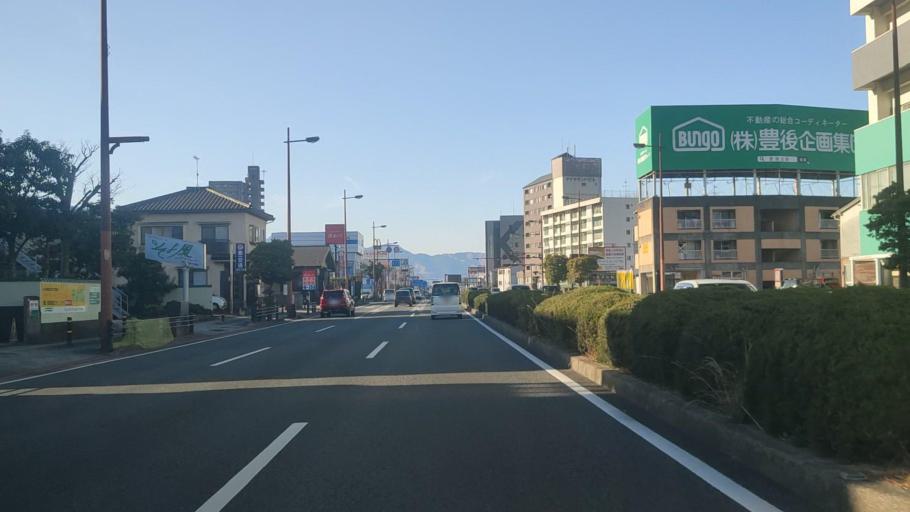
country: JP
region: Oita
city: Oita
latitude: 33.2443
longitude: 131.5869
